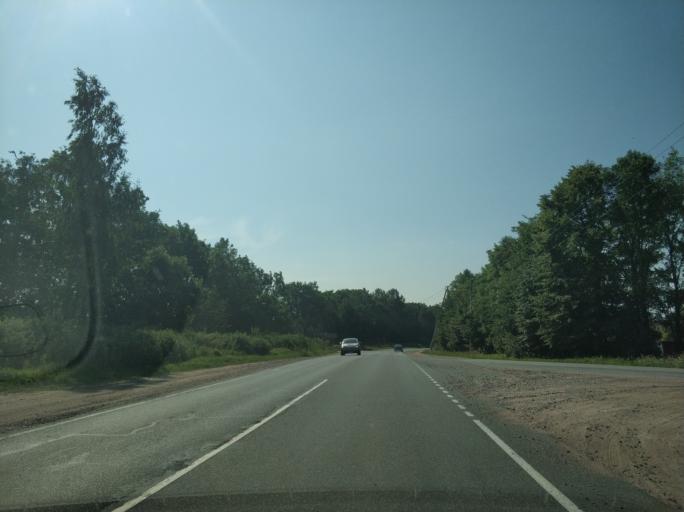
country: RU
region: Leningrad
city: Romanovka
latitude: 60.0606
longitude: 30.7423
